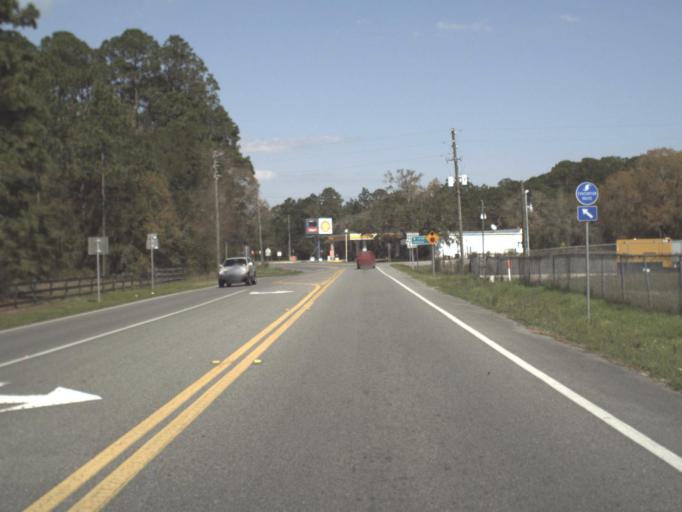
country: US
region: Florida
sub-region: Wakulla County
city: Crawfordville
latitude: 30.0824
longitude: -84.3903
